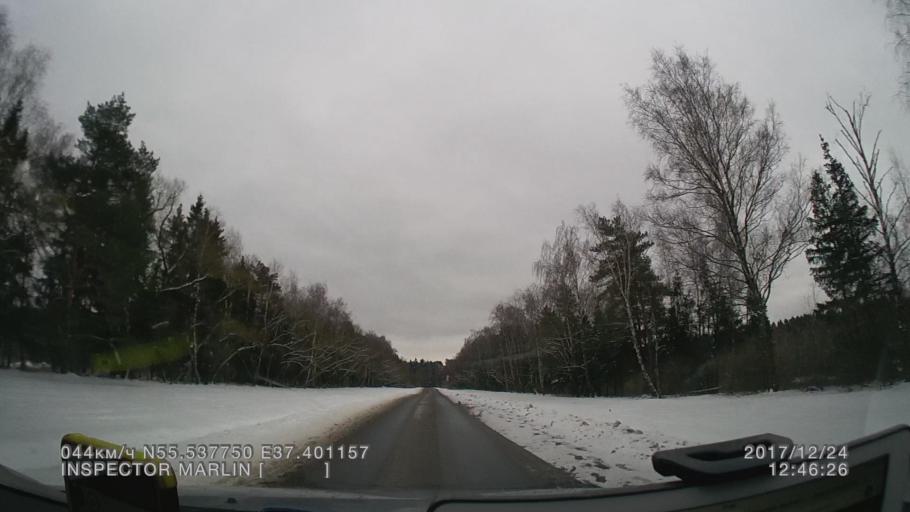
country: RU
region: Moskovskaya
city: Filimonki
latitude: 55.5377
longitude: 37.4012
